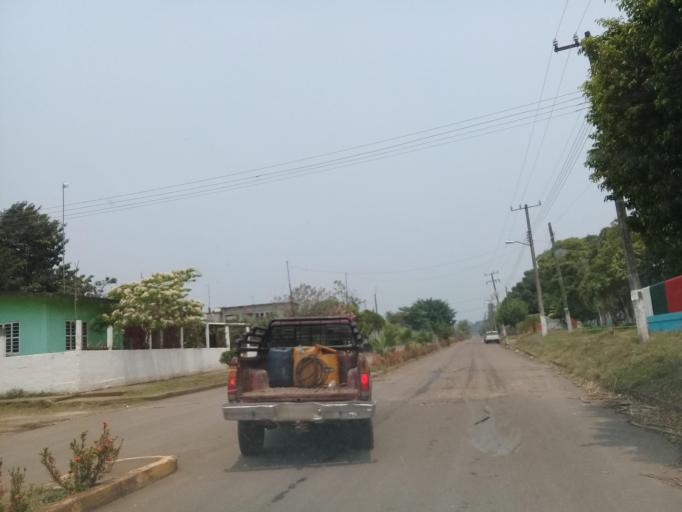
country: MX
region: Veracruz
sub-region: Tezonapa
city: Laguna Chica (Pueblo Nuevo)
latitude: 18.5157
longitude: -96.7182
